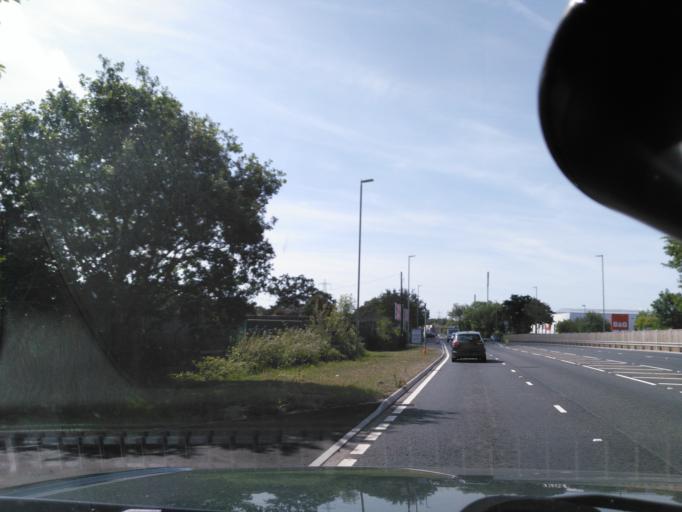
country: GB
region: England
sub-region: Hampshire
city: Botley
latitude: 50.8650
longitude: -1.2552
